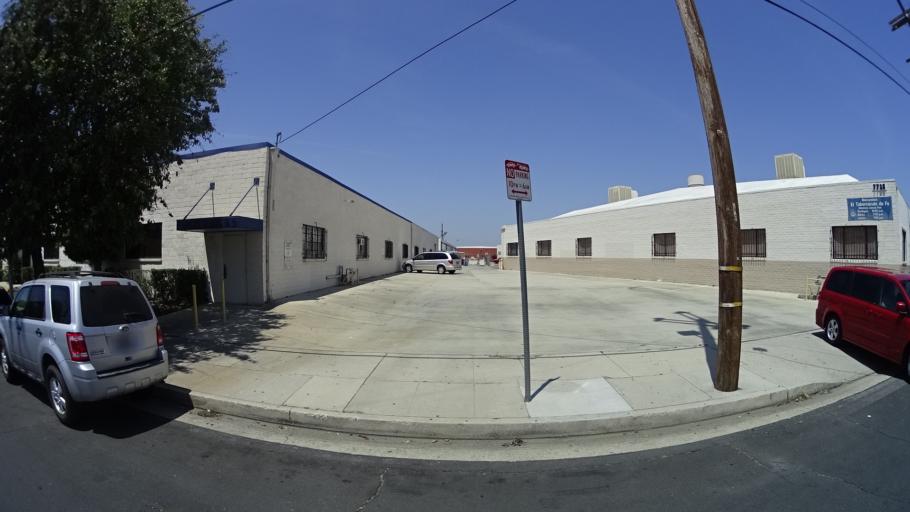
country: US
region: California
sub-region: Los Angeles County
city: Van Nuys
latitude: 34.2111
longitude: -118.4575
